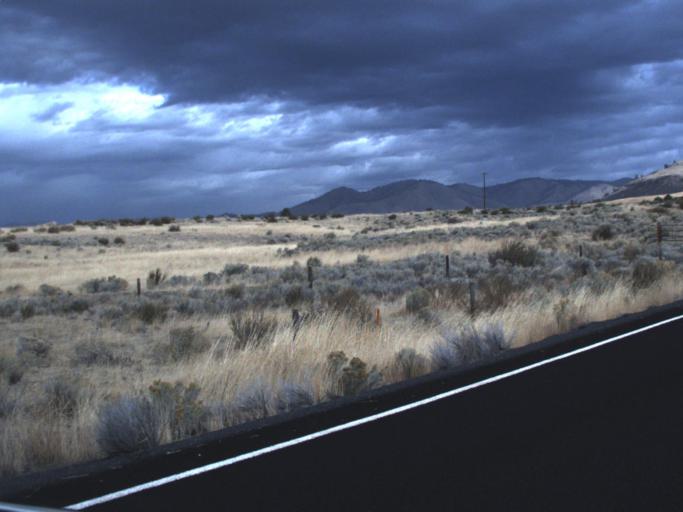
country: US
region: Washington
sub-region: Okanogan County
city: Coulee Dam
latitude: 47.9000
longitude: -118.7020
